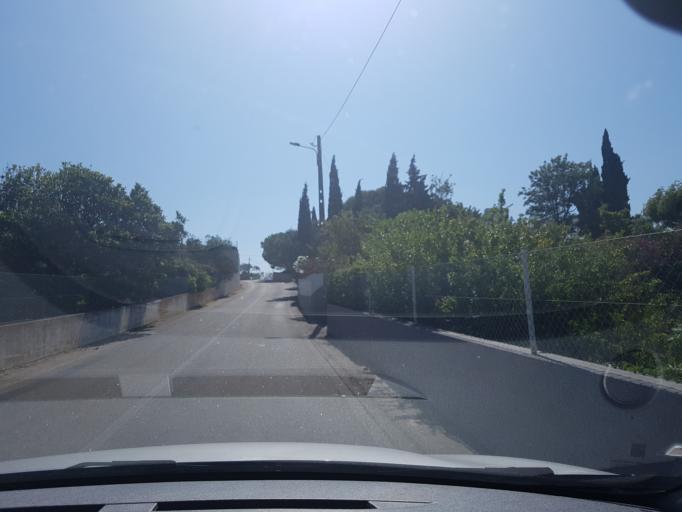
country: PT
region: Faro
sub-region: Lagoa
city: Carvoeiro
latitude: 37.0973
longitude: -8.4207
